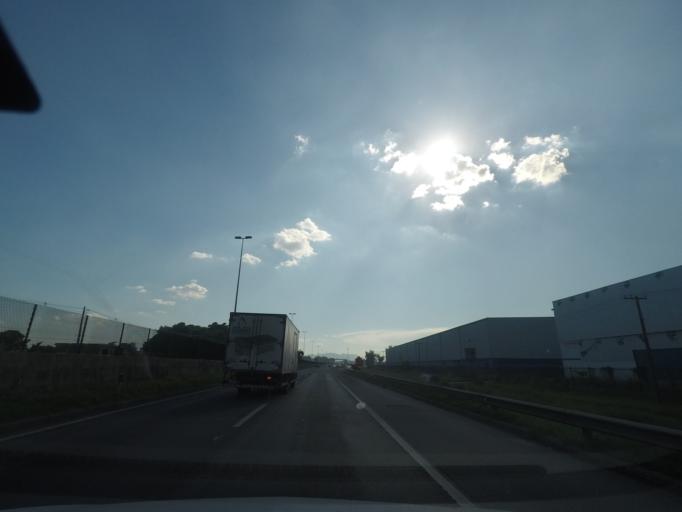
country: BR
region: Rio de Janeiro
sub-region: Duque De Caxias
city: Duque de Caxias
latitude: -22.6636
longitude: -43.2576
